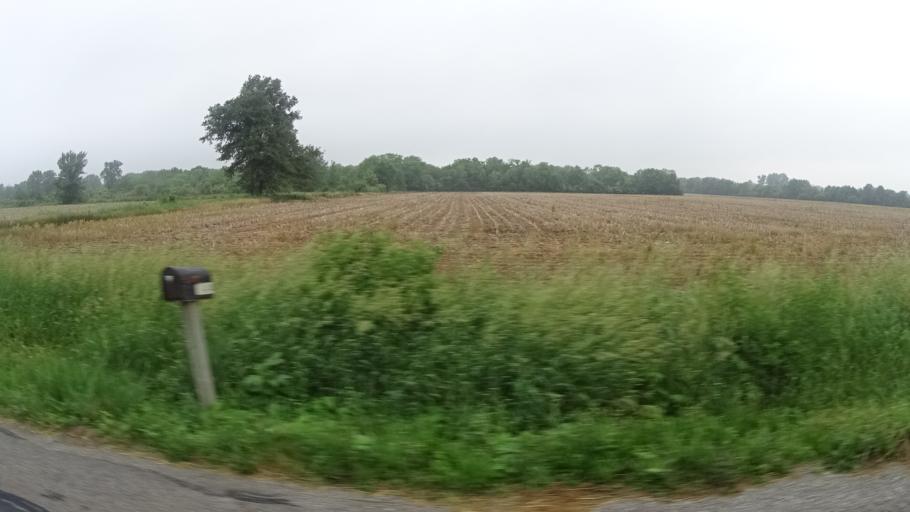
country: US
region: Ohio
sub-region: Huron County
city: Bellevue
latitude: 41.3621
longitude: -82.8037
